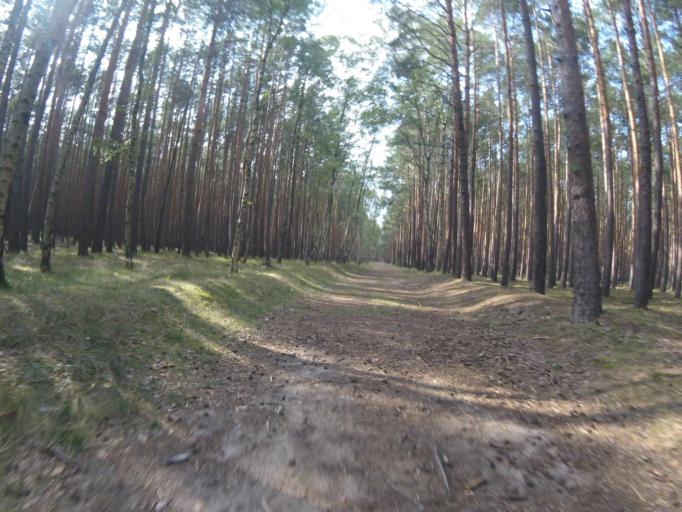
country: DE
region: Brandenburg
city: Gross Koris
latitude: 52.2213
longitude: 13.7530
